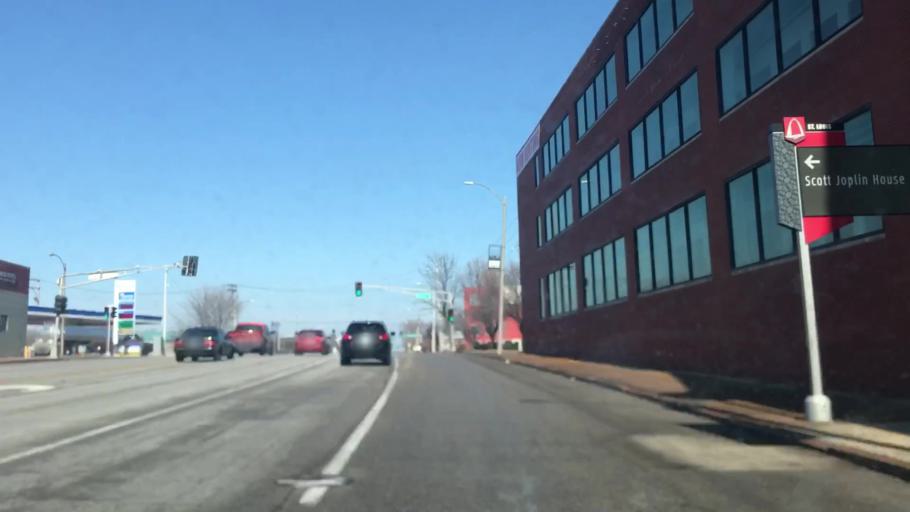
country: US
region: Missouri
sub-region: City of Saint Louis
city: St. Louis
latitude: 38.6363
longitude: -90.2127
